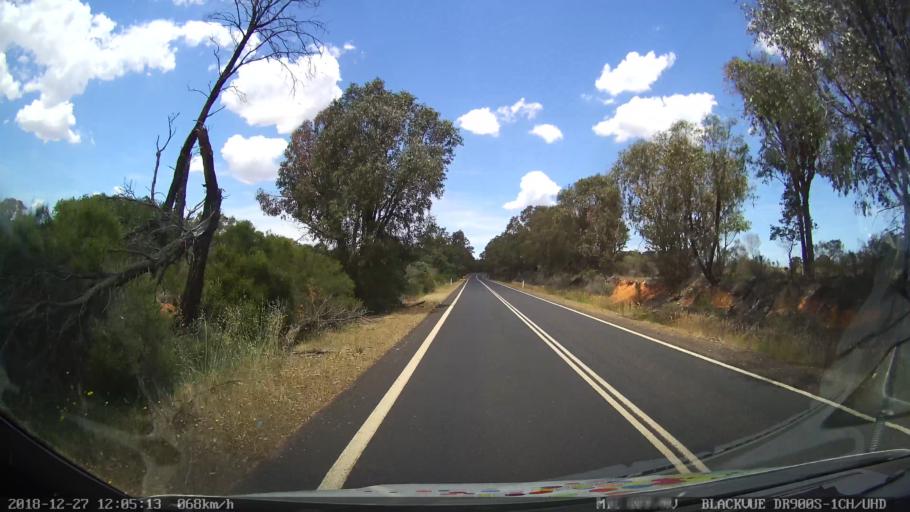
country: AU
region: New South Wales
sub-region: Blayney
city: Blayney
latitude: -33.8010
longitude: 149.3412
